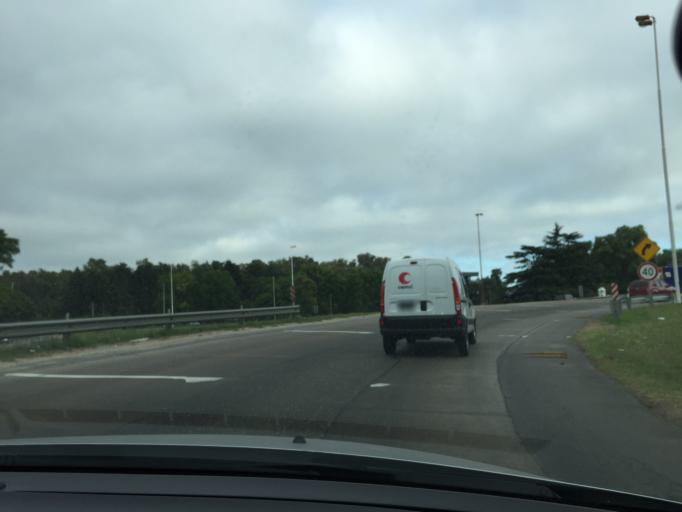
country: AR
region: Buenos Aires
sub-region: Partido de Ezeiza
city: Ezeiza
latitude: -34.7847
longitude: -58.5262
